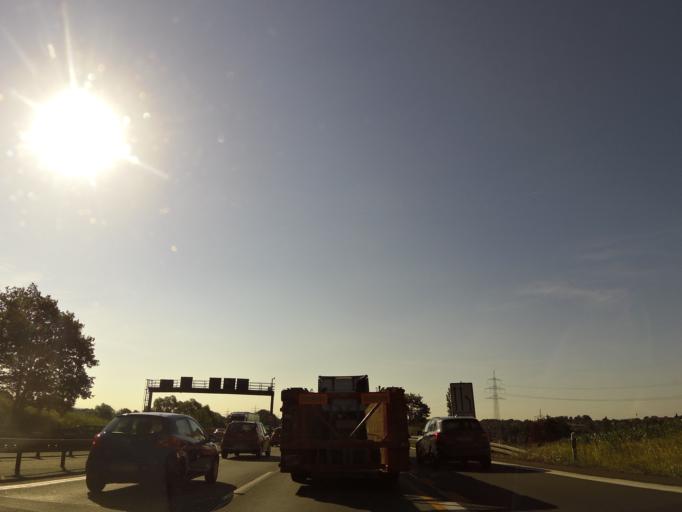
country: DE
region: Bavaria
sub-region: Regierungsbezirk Mittelfranken
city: Obermichelbach
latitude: 49.5649
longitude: 10.9468
